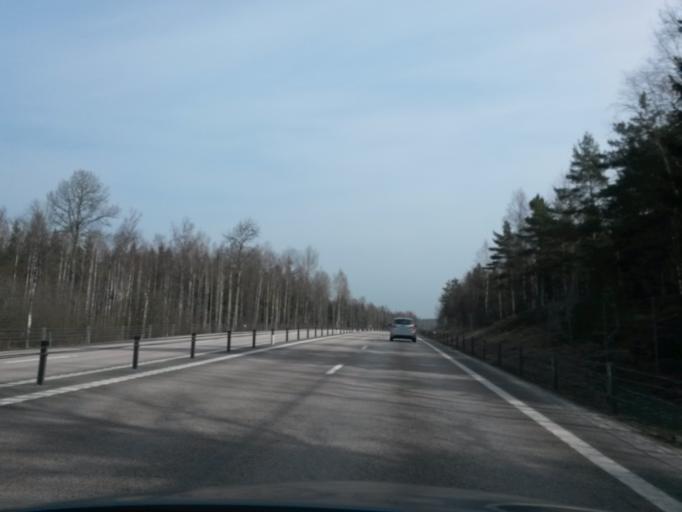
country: SE
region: Vaestra Goetaland
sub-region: Toreboda Kommun
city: Toereboda
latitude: 58.7709
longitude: 13.9916
